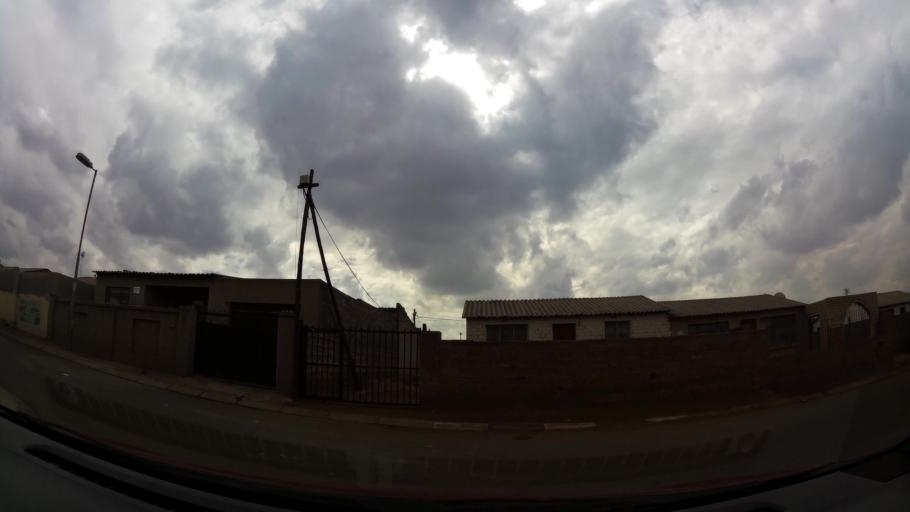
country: ZA
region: Gauteng
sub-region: City of Johannesburg Metropolitan Municipality
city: Soweto
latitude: -26.2561
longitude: 27.8353
